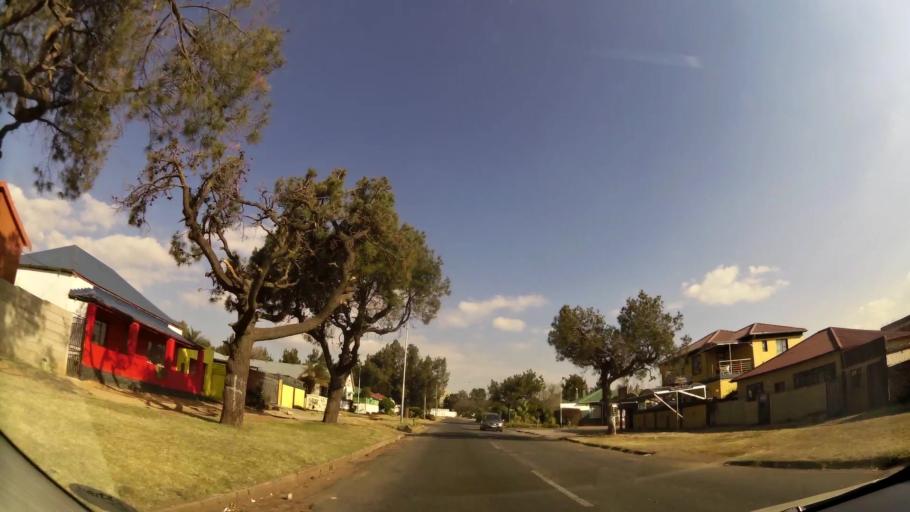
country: ZA
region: Gauteng
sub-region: West Rand District Municipality
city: Krugersdorp
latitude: -26.1026
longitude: 27.7682
